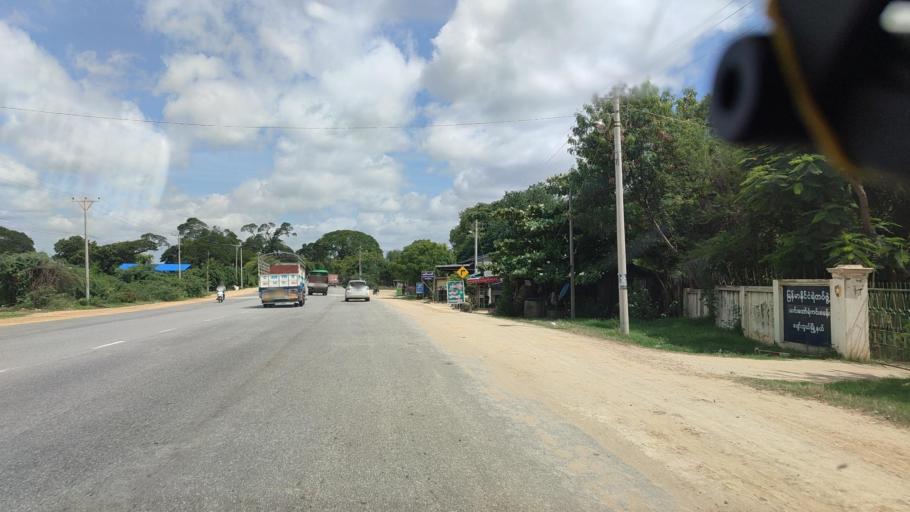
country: MM
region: Mandalay
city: Meiktila
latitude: 20.7108
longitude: 95.9411
